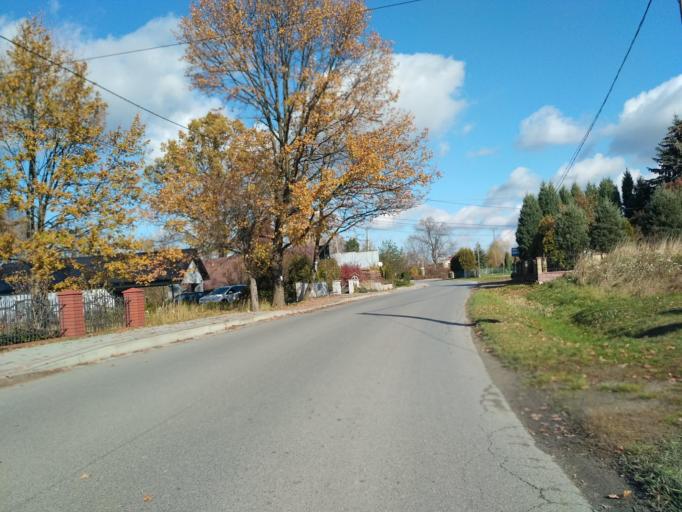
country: PL
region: Subcarpathian Voivodeship
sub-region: Powiat rzeszowski
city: Glogow Malopolski
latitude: 50.1345
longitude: 21.9031
